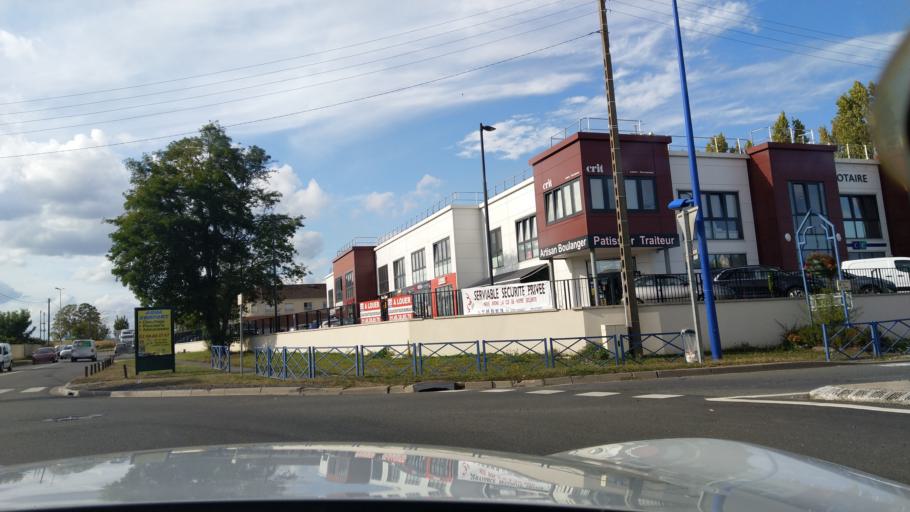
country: FR
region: Picardie
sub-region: Departement de l'Oise
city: Lagny-le-Sec
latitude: 49.0941
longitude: 2.7467
